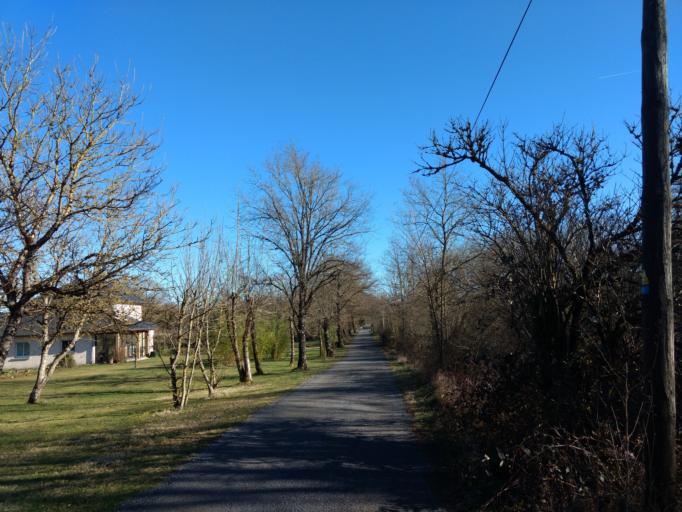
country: FR
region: Midi-Pyrenees
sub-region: Departement de l'Aveyron
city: Sebazac-Concoures
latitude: 44.4171
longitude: 2.5689
